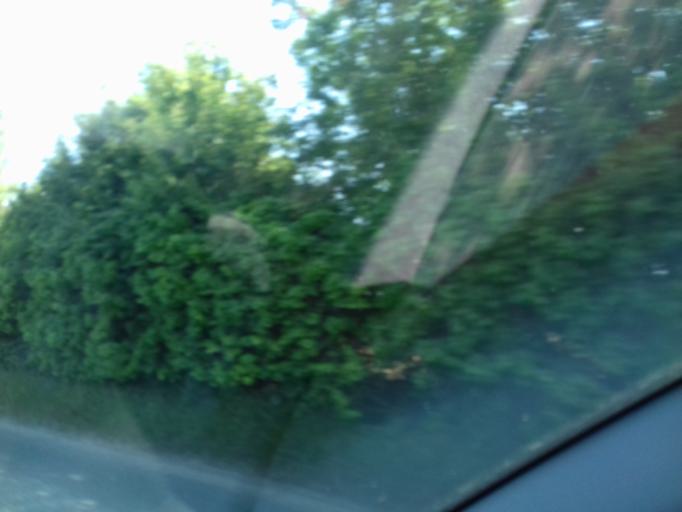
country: IE
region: Leinster
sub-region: An Mhi
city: Stamullin
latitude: 53.5979
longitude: -6.2457
